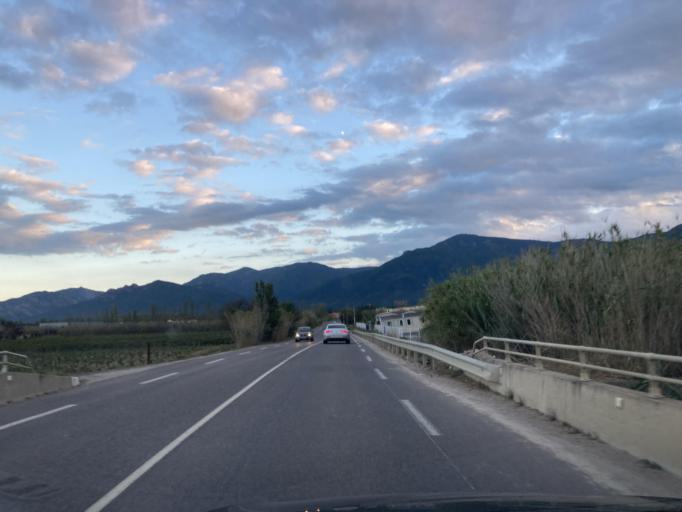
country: FR
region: Languedoc-Roussillon
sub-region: Departement des Pyrenees-Orientales
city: Sant Genis de Fontanes
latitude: 42.5535
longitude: 2.9143
